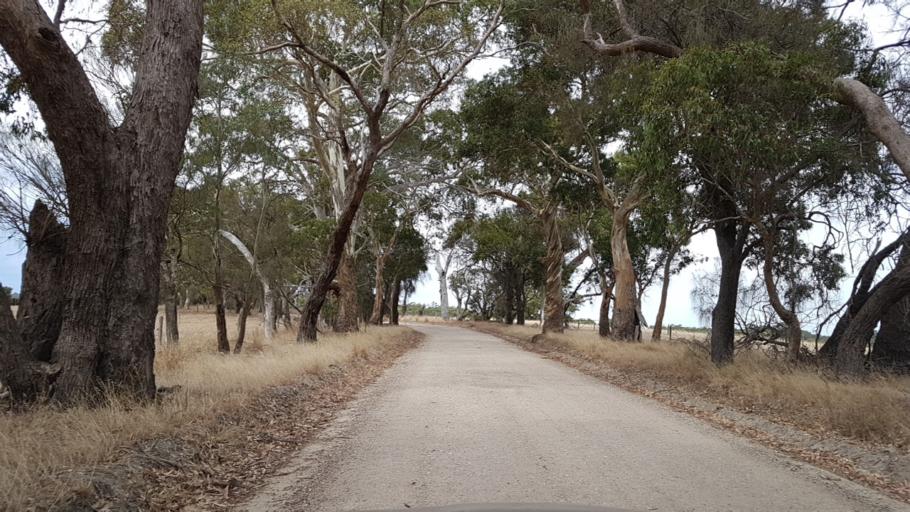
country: AU
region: South Australia
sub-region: Adelaide Hills
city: Birdwood
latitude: -34.7621
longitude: 139.0012
